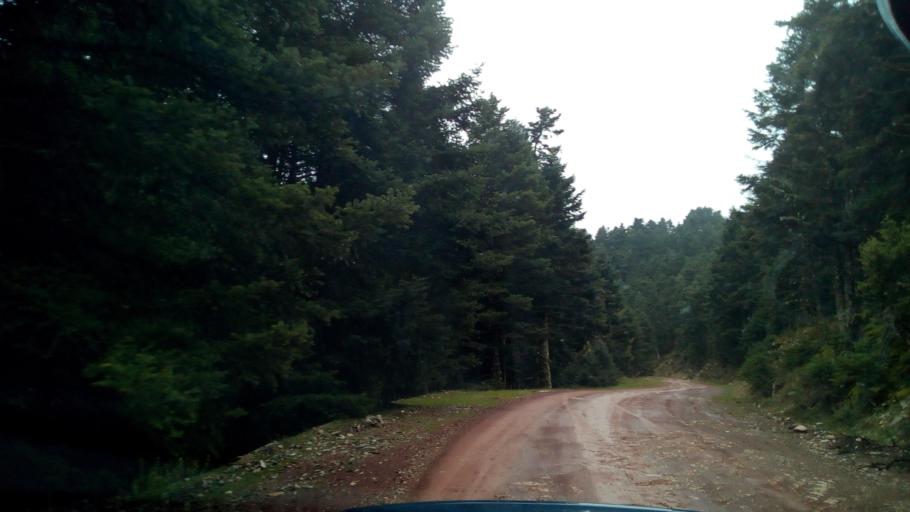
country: GR
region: West Greece
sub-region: Nomos Aitolias kai Akarnanias
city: Nafpaktos
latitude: 38.5396
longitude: 21.8584
